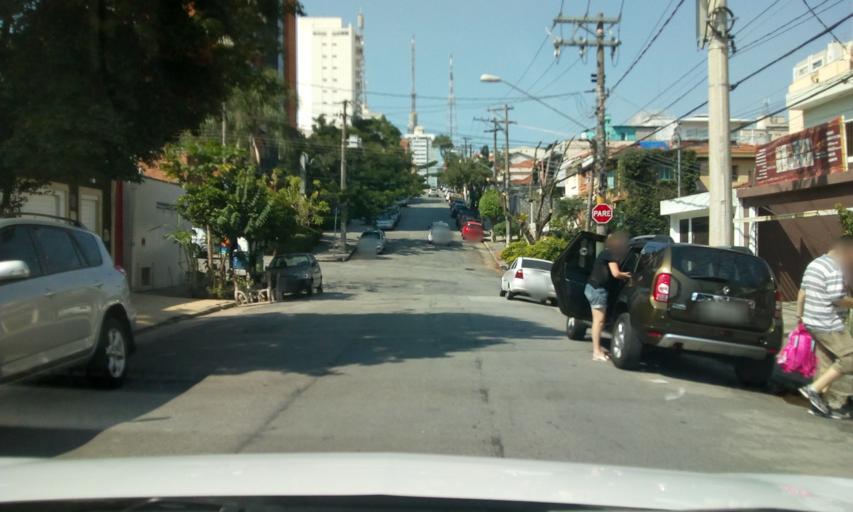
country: BR
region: Sao Paulo
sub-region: Sao Paulo
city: Sao Paulo
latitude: -23.5411
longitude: -46.6874
